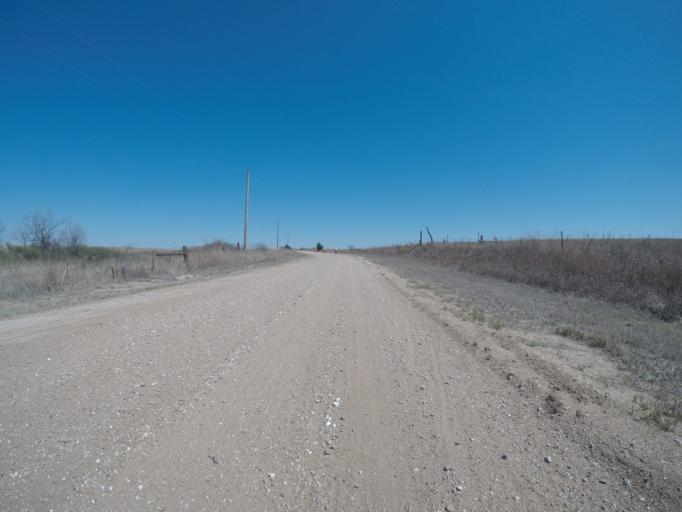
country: US
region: Kansas
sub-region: Pratt County
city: Pratt
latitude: 37.4160
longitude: -98.8387
